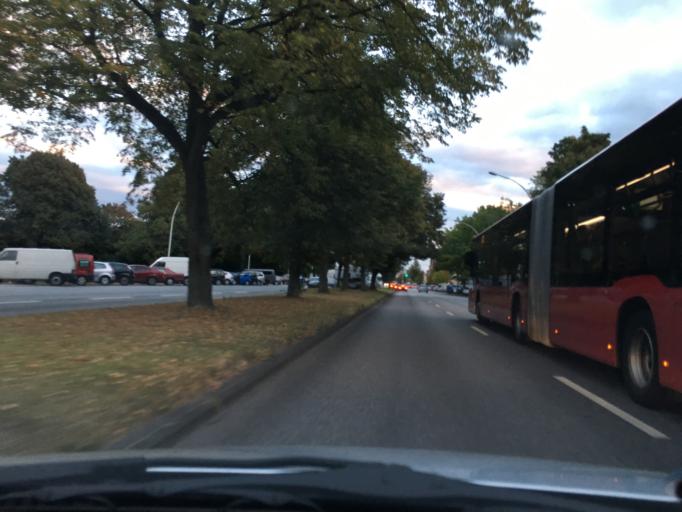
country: DE
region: Schleswig-Holstein
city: Kiel
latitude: 54.3299
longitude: 10.1159
